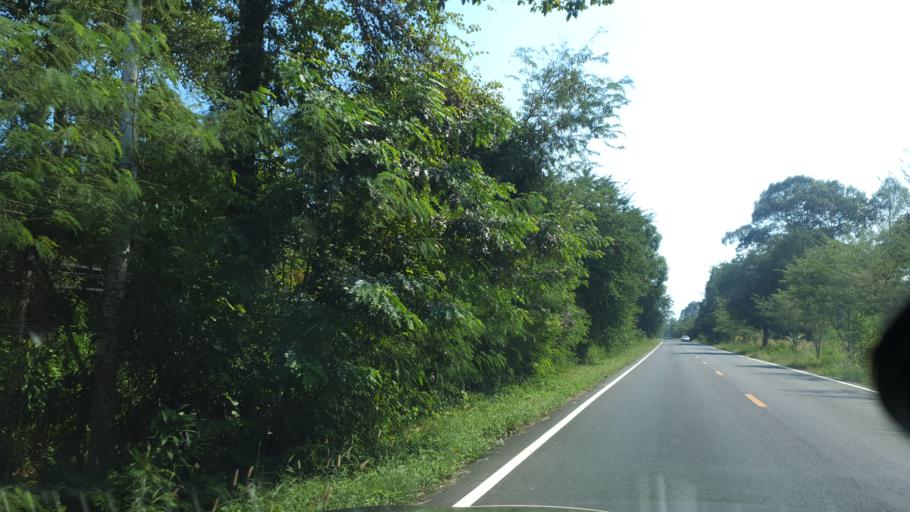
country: TH
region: Surat Thani
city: Tha Chana
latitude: 9.5819
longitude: 99.2028
